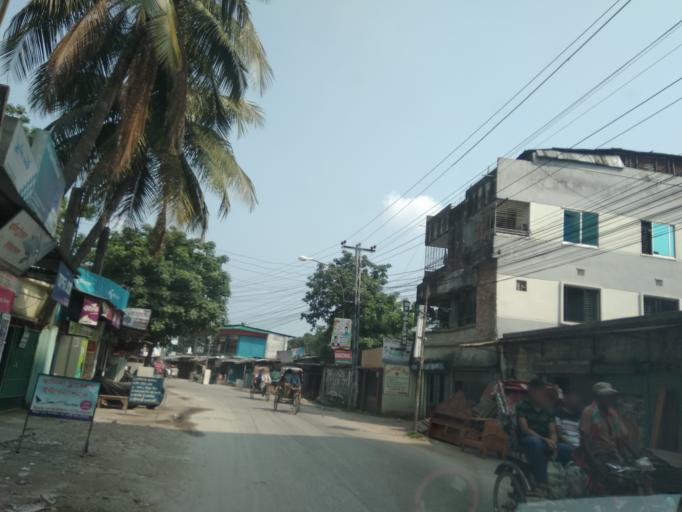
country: BD
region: Rangpur Division
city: Rangpur
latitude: 25.7594
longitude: 89.2328
